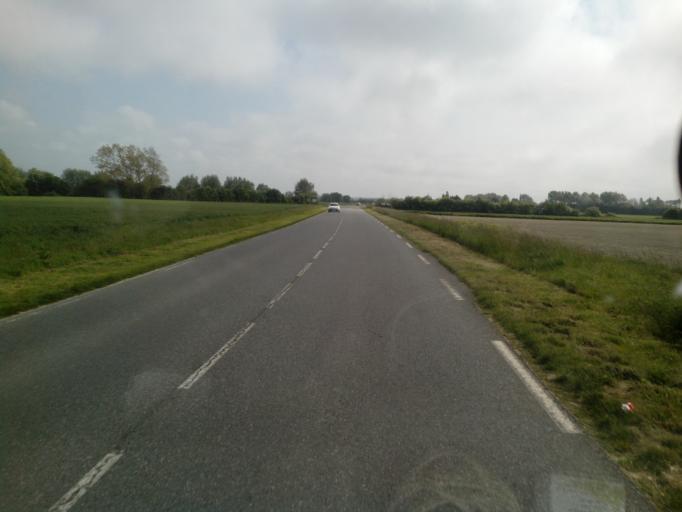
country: FR
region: Picardie
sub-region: Departement de la Somme
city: Le Crotoy
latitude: 50.2361
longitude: 1.6448
